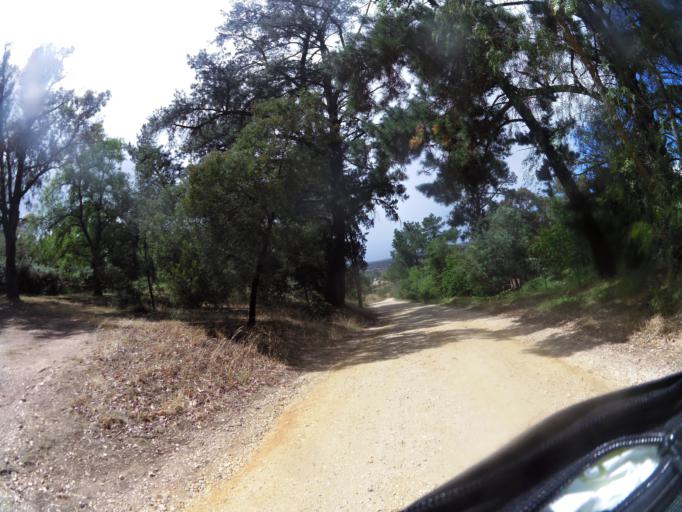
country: AU
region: Victoria
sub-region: Mount Alexander
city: Castlemaine
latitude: -37.0660
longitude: 144.2266
